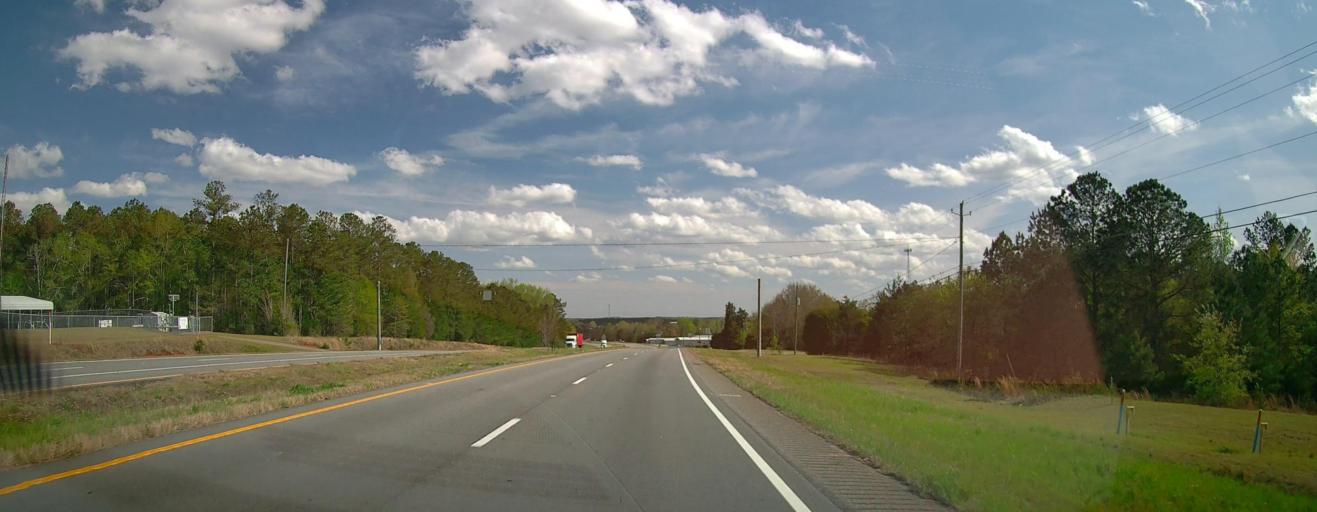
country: US
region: Georgia
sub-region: Baldwin County
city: Hardwick
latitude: 33.0170
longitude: -83.2275
